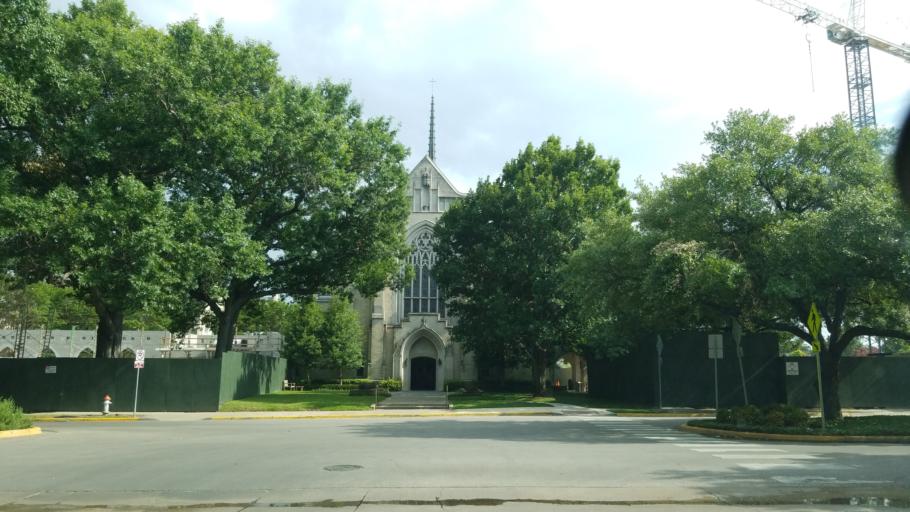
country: US
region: Texas
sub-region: Dallas County
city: University Park
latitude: 32.8455
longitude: -96.8000
